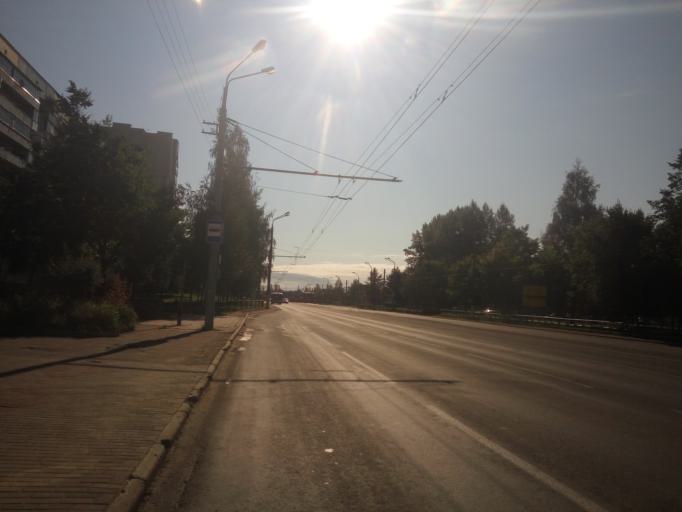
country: BY
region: Vitebsk
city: Vitebsk
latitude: 55.1688
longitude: 30.2379
